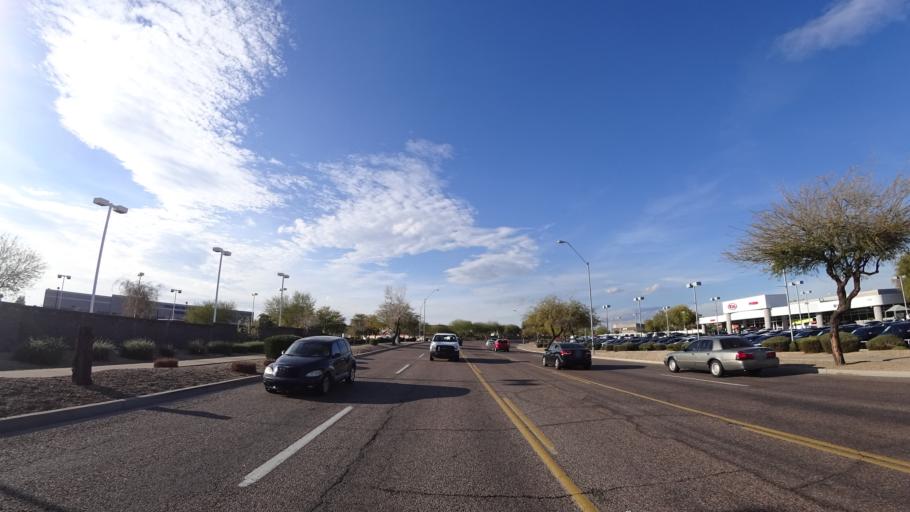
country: US
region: Arizona
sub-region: Maricopa County
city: Sun City
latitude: 33.6411
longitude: -112.2541
